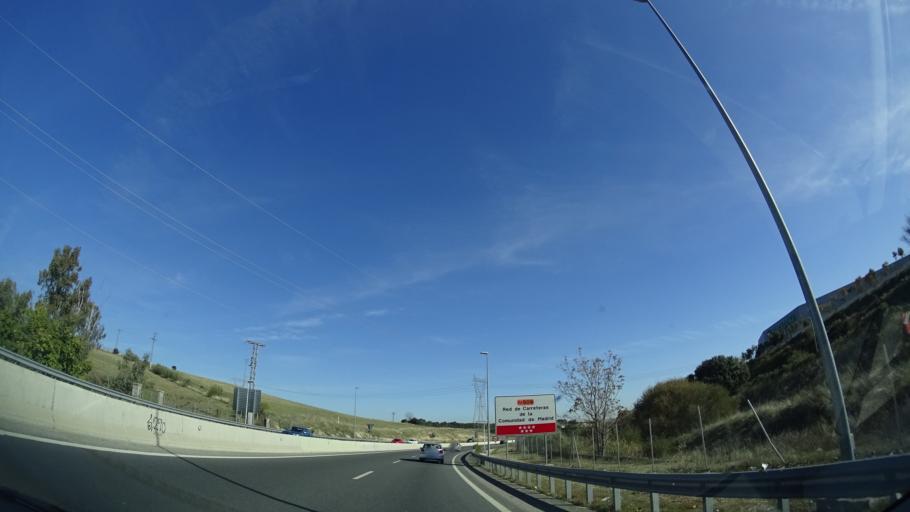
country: ES
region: Madrid
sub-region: Provincia de Madrid
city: Villanueva del Pardillo
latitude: 40.4911
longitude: -3.9559
